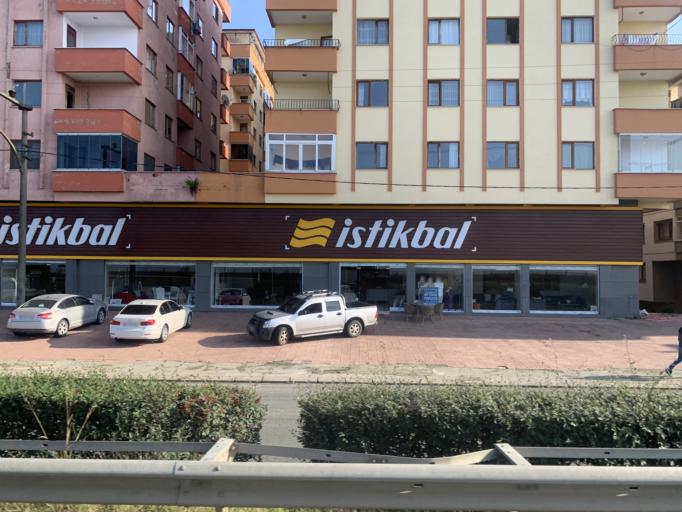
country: TR
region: Trabzon
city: Of
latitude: 40.9416
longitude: 40.2587
